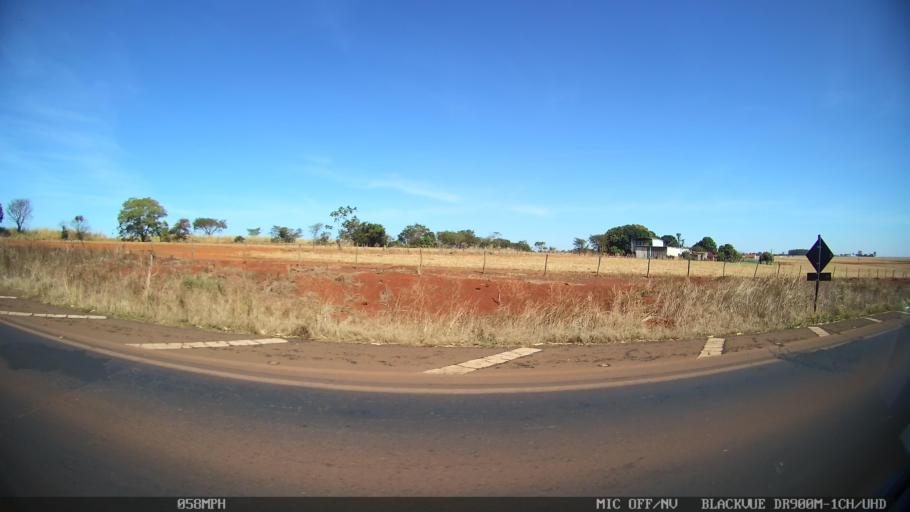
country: BR
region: Sao Paulo
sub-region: Sao Joaquim Da Barra
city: Sao Joaquim da Barra
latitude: -20.5215
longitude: -47.8601
